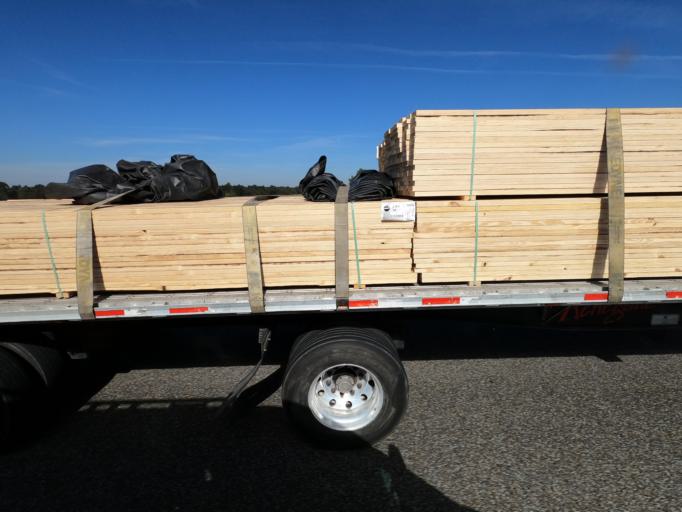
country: US
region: Tennessee
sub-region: Crockett County
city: Bells
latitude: 35.5878
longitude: -89.0850
